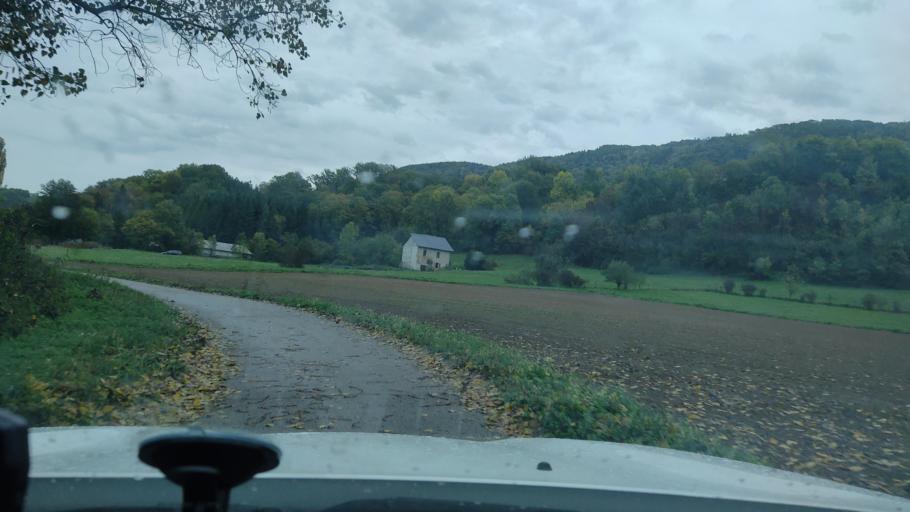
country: FR
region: Rhone-Alpes
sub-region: Departement de la Savoie
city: Cruet
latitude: 45.5013
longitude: 6.1103
